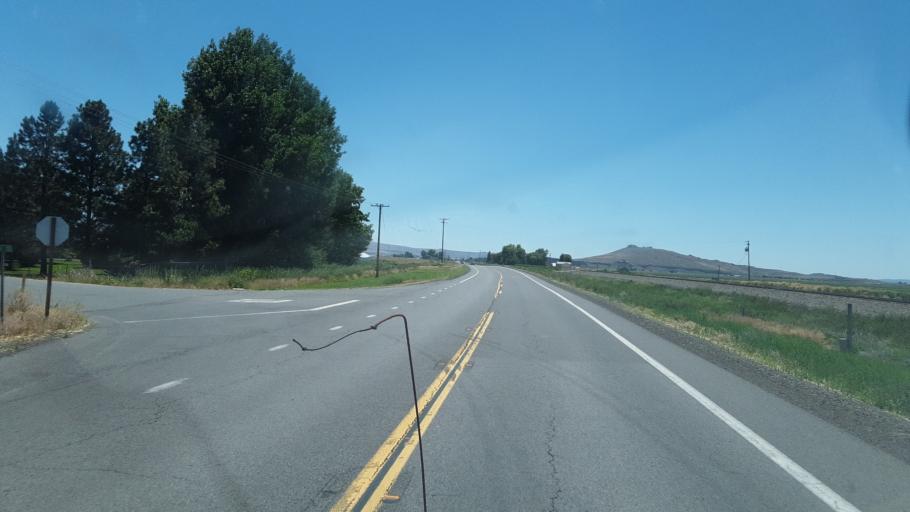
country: US
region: California
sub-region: Siskiyou County
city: Tulelake
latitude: 41.9219
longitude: -121.4346
